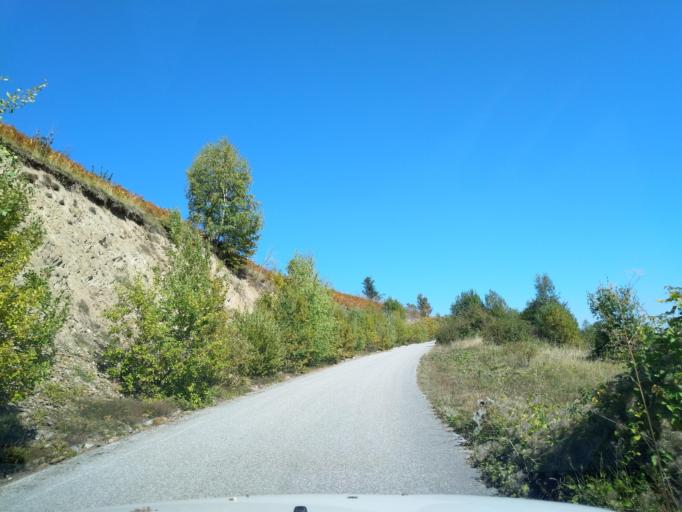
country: RS
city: Sokolovica
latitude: 43.2507
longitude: 20.3296
